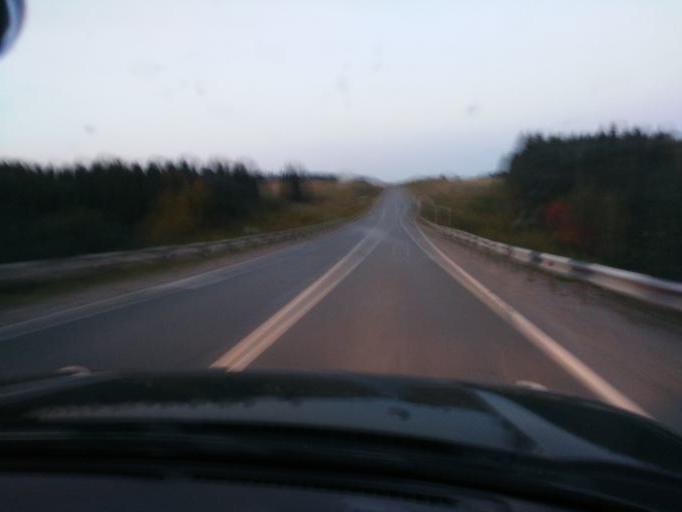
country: RU
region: Perm
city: Verkhnechusovskiye Gorodki
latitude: 58.2232
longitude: 57.1840
